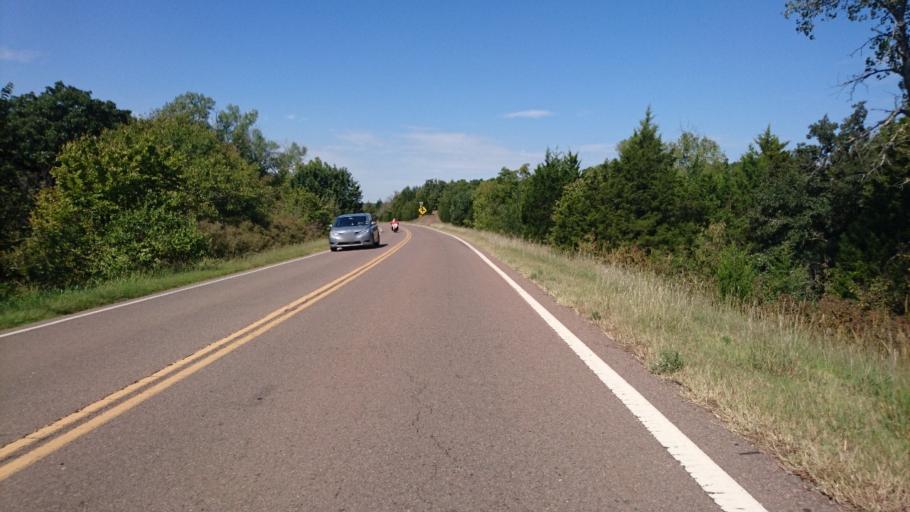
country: US
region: Oklahoma
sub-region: Oklahoma County
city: Jones
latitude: 35.6659
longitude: -97.2970
